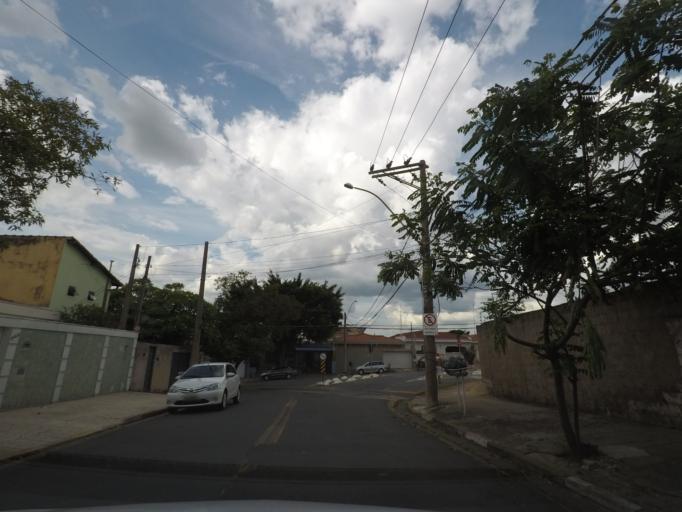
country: BR
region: Sao Paulo
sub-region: Campinas
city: Campinas
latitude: -22.8944
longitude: -47.1010
